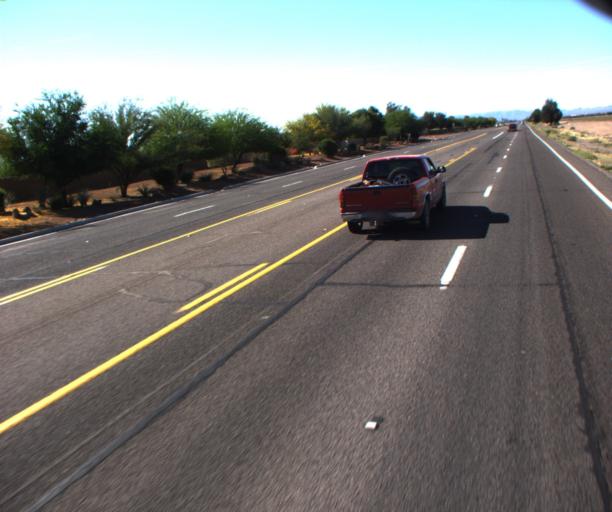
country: US
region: Arizona
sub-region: Mohave County
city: Mohave Valley
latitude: 34.9625
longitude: -114.5980
